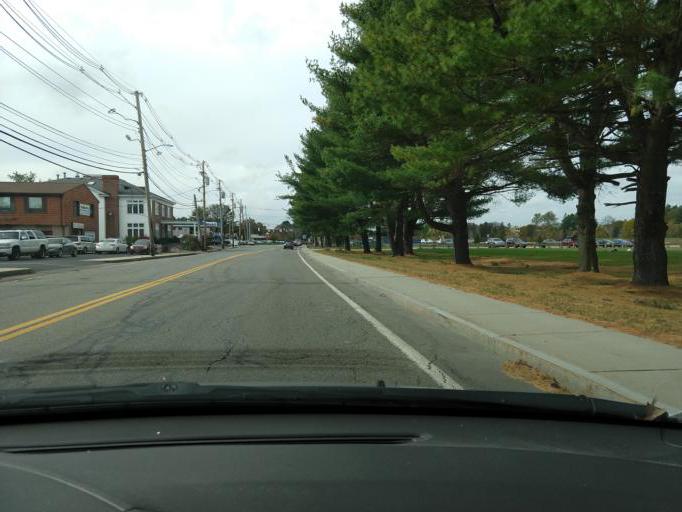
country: US
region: Massachusetts
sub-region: Middlesex County
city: Pinehurst
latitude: 42.5018
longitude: -71.2316
